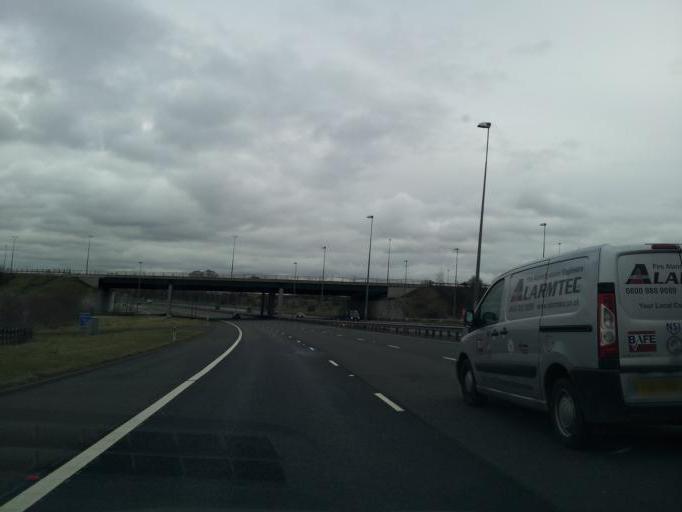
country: GB
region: England
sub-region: Staffordshire
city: Essington
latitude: 52.6648
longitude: -2.0622
